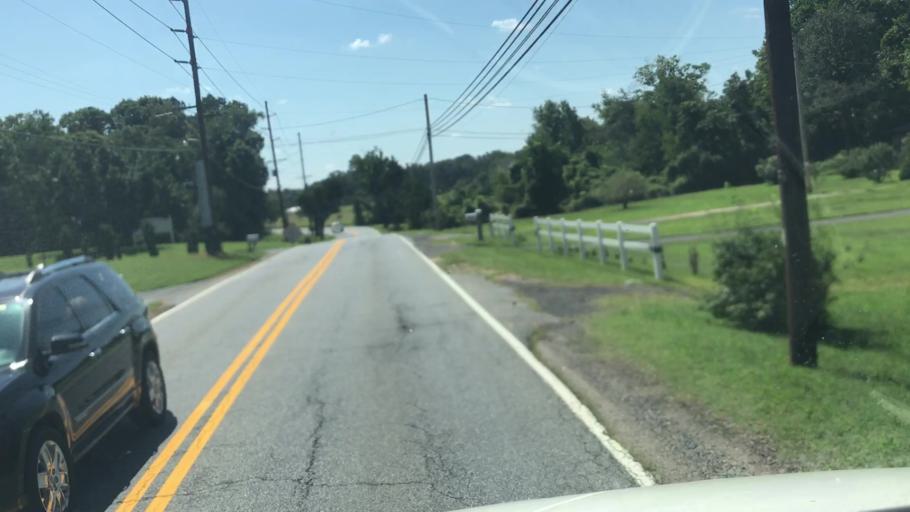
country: US
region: Maryland
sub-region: Prince George's County
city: Clinton
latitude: 38.7197
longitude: -76.8922
